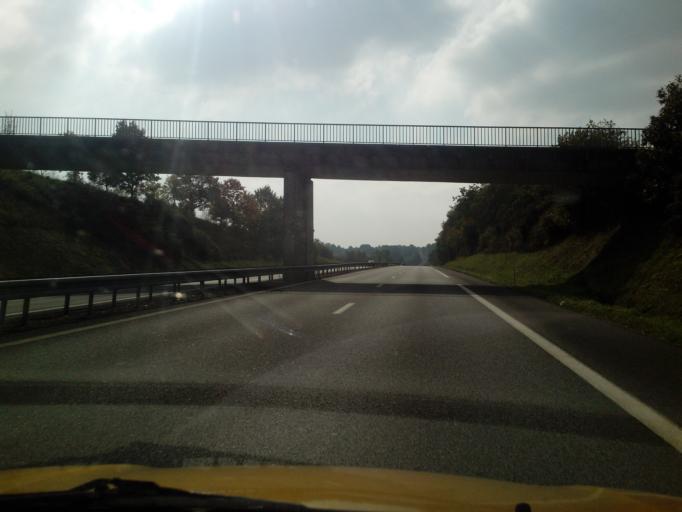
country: FR
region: Brittany
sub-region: Departement du Morbihan
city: Ploermel
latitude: 47.8850
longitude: -2.4157
